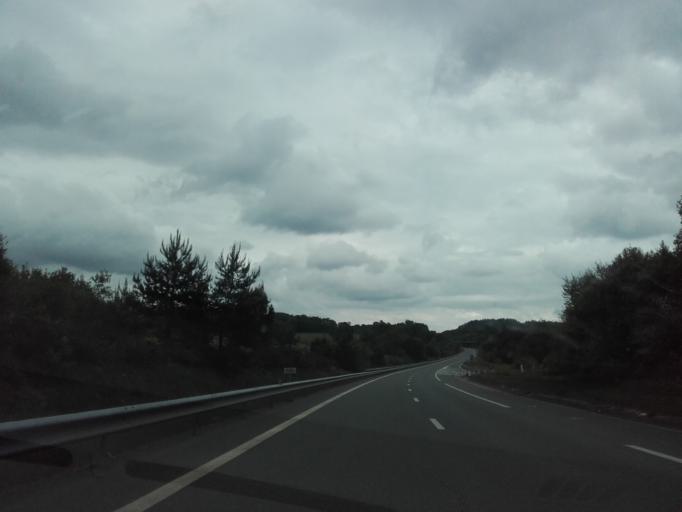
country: FR
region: Limousin
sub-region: Departement de la Correze
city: Correze
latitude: 45.3621
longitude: 1.9394
